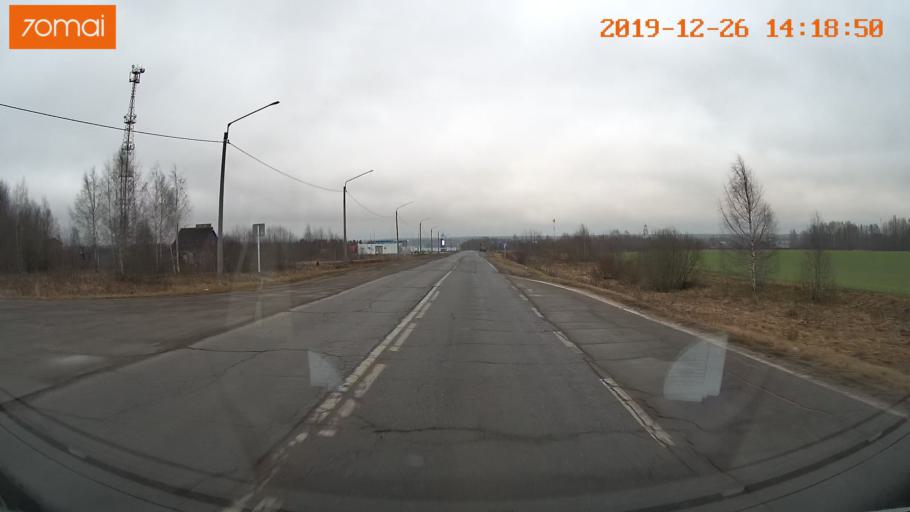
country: RU
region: Jaroslavl
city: Poshekhon'ye
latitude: 58.5132
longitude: 39.1049
